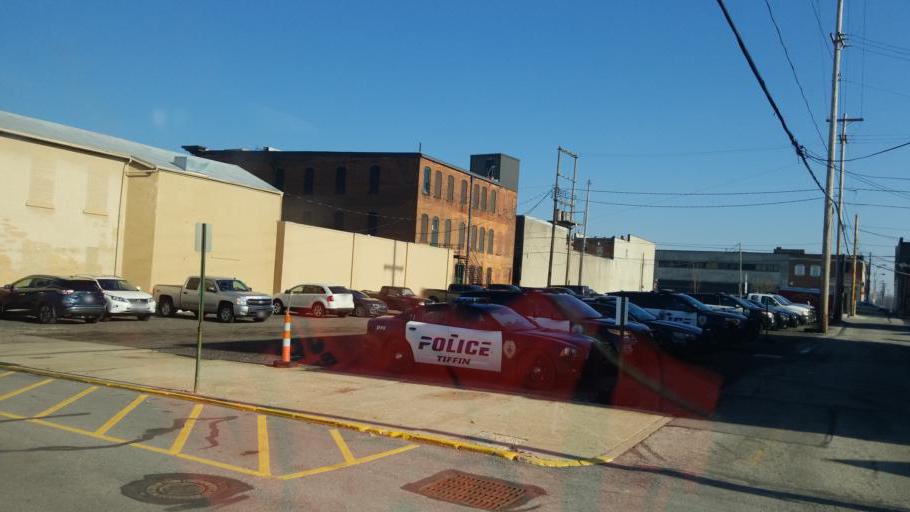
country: US
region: Ohio
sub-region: Seneca County
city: Tiffin
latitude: 41.1151
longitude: -83.1783
